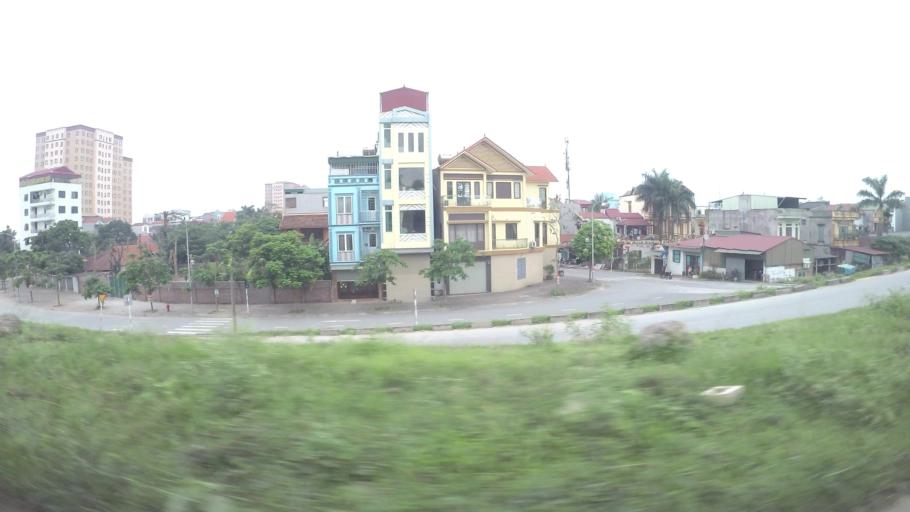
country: VN
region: Ha Noi
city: Trau Quy
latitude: 21.0584
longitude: 105.9189
